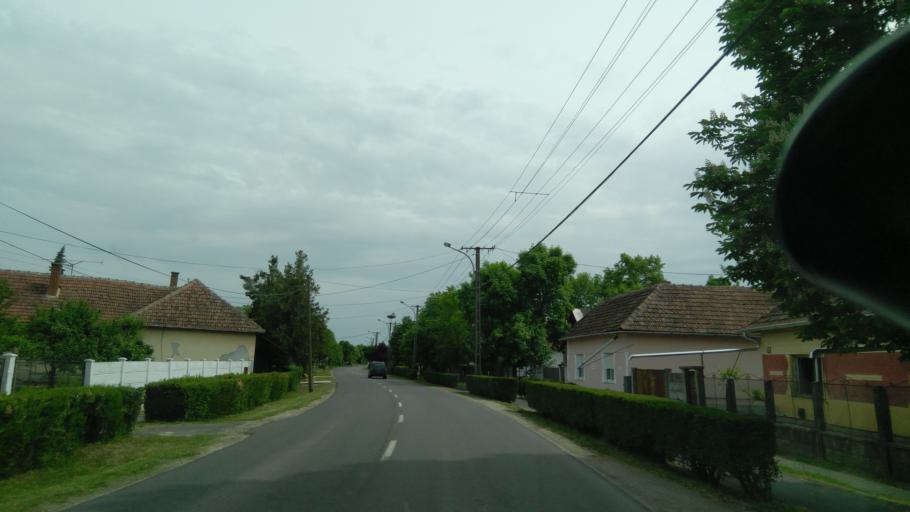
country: HU
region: Bekes
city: Sarkad
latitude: 46.8070
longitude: 21.3809
